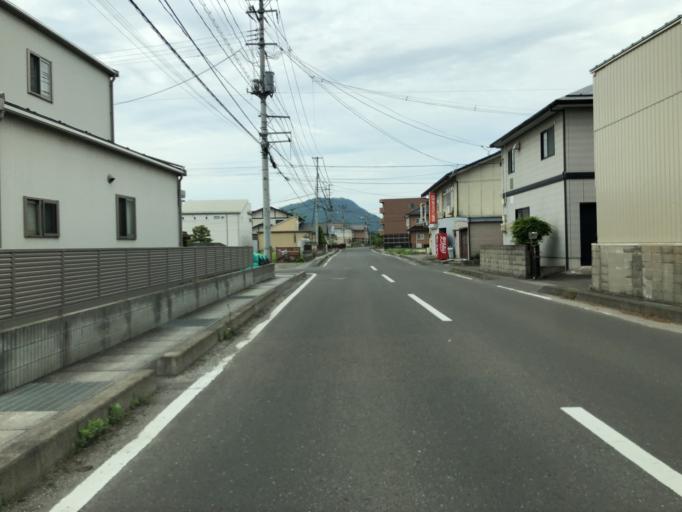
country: JP
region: Fukushima
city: Fukushima-shi
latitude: 37.7917
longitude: 140.4590
